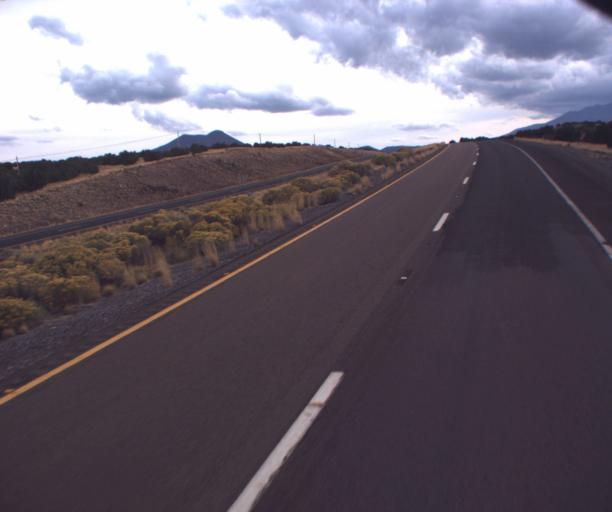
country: US
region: Arizona
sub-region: Coconino County
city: Flagstaff
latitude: 35.4934
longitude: -111.5546
